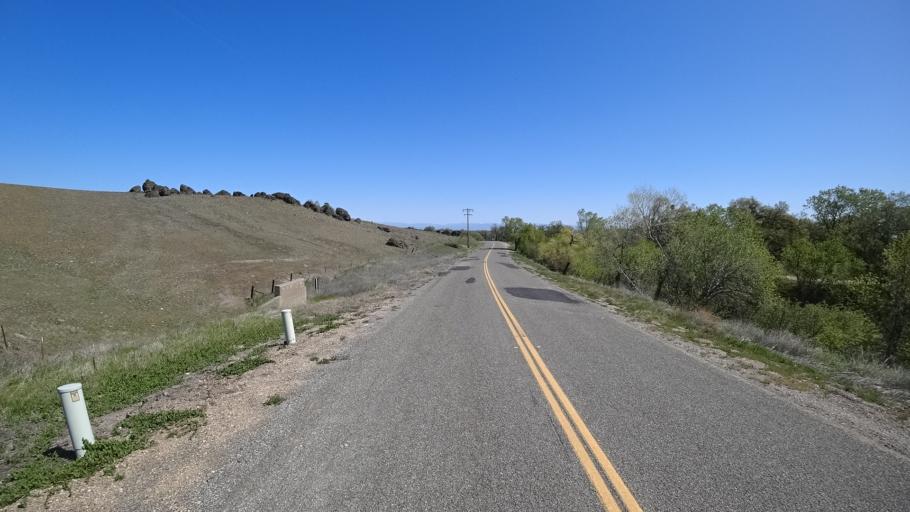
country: US
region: California
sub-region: Glenn County
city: Orland
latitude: 39.7662
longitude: -122.3300
